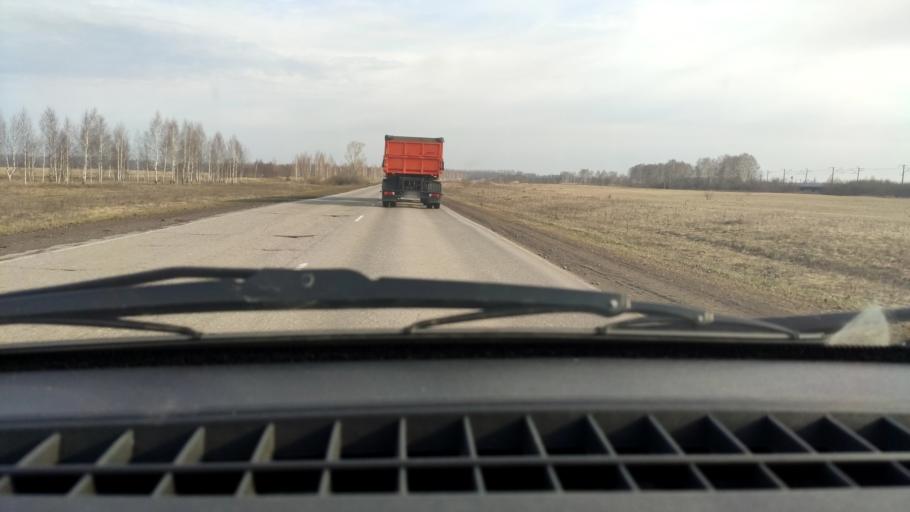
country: RU
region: Bashkortostan
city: Chishmy
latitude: 54.4315
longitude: 55.2348
